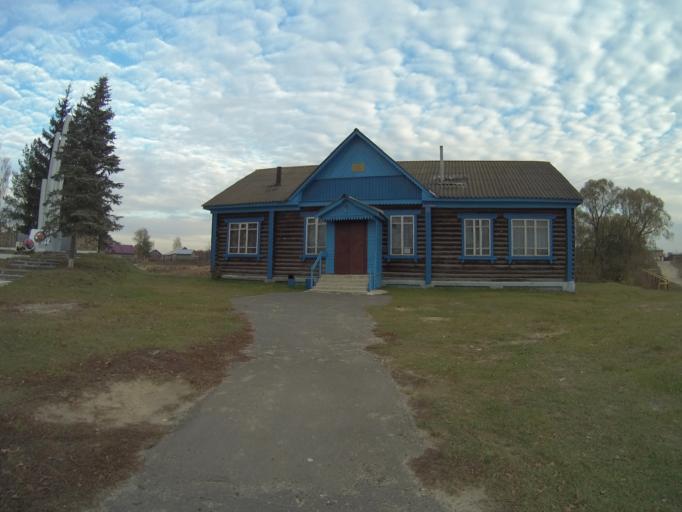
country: RU
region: Vladimir
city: Orgtrud
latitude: 56.1565
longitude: 40.5995
